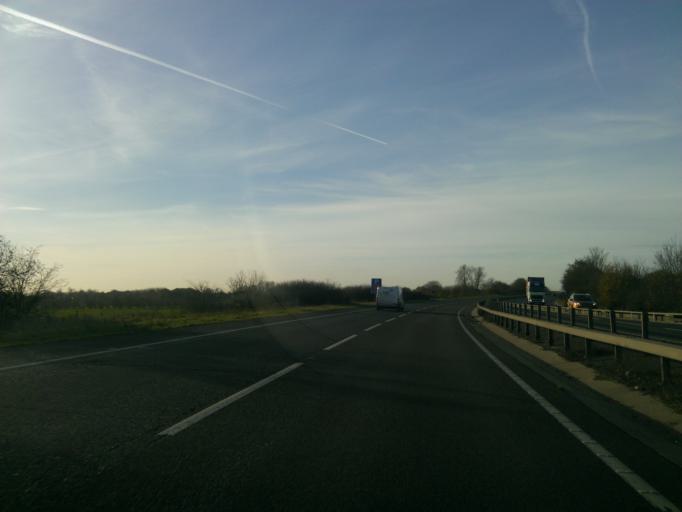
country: GB
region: England
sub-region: Essex
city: Witham
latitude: 51.7915
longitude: 0.6490
